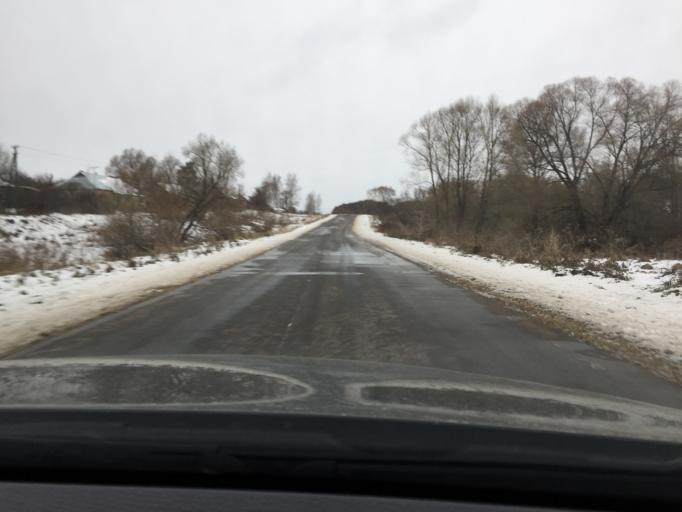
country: RU
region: Tula
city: Shchekino
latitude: 53.8182
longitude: 37.5604
